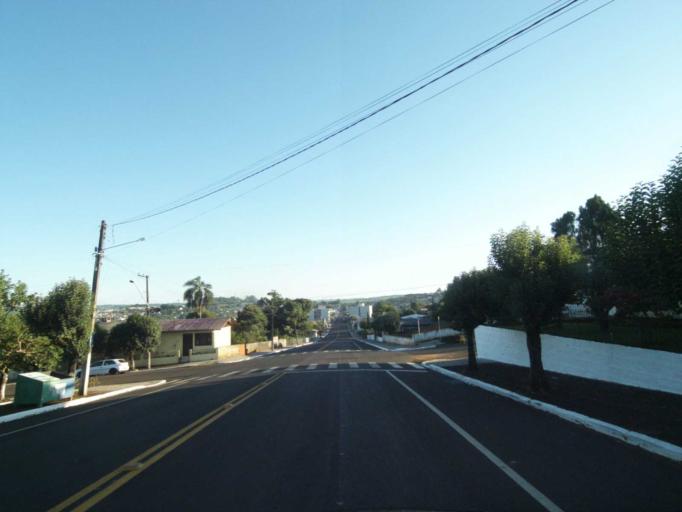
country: BR
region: Parana
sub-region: Coronel Vivida
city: Coronel Vivida
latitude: -25.9594
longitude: -52.8168
